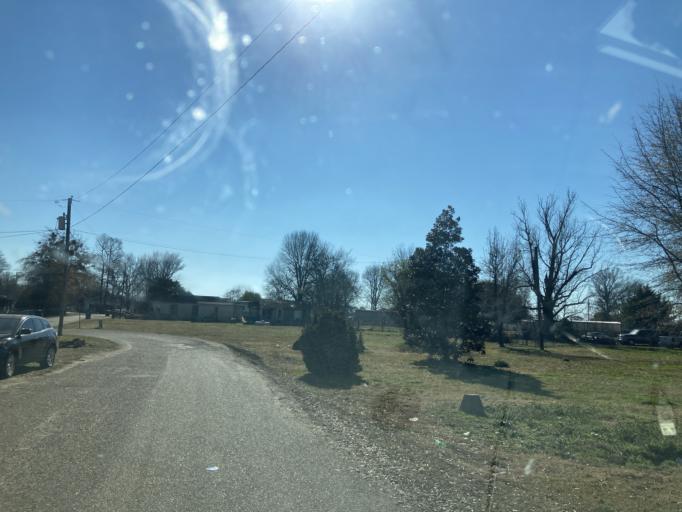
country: US
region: Mississippi
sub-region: Yazoo County
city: Yazoo City
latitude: 32.9771
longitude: -90.5929
